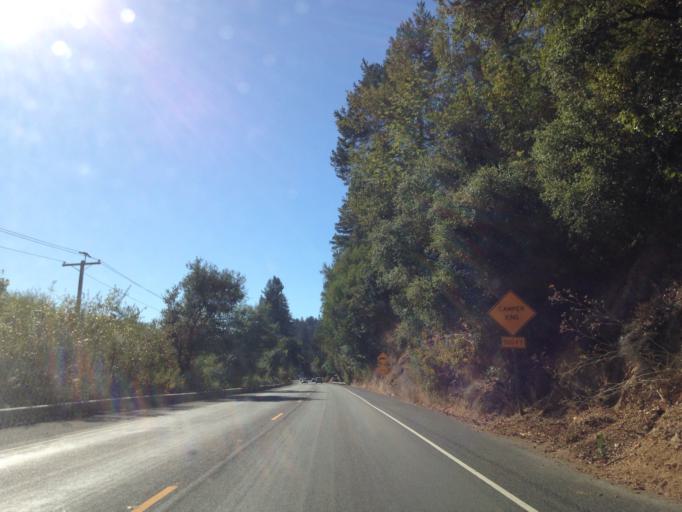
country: US
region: California
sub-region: Sonoma County
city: Guerneville
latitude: 38.5063
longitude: -122.9532
